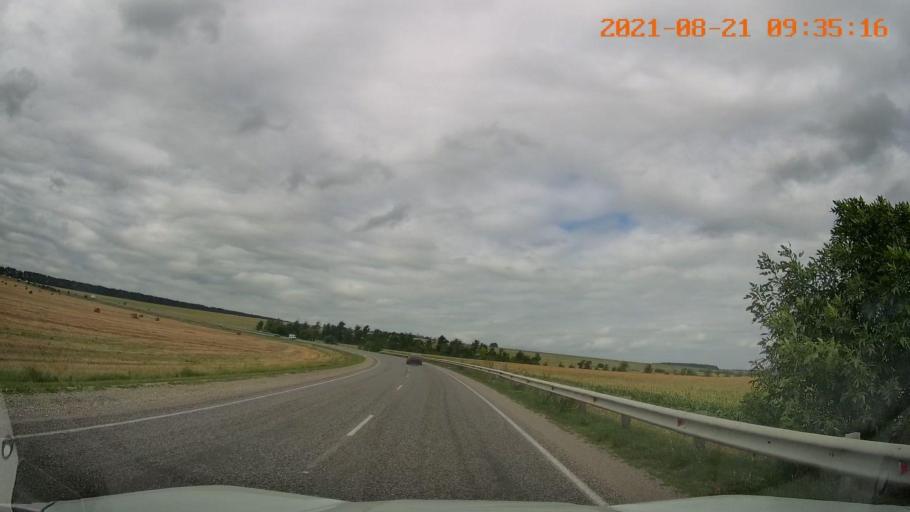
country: RU
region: Stavropol'skiy
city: Yutsa
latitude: 43.9922
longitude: 42.9583
